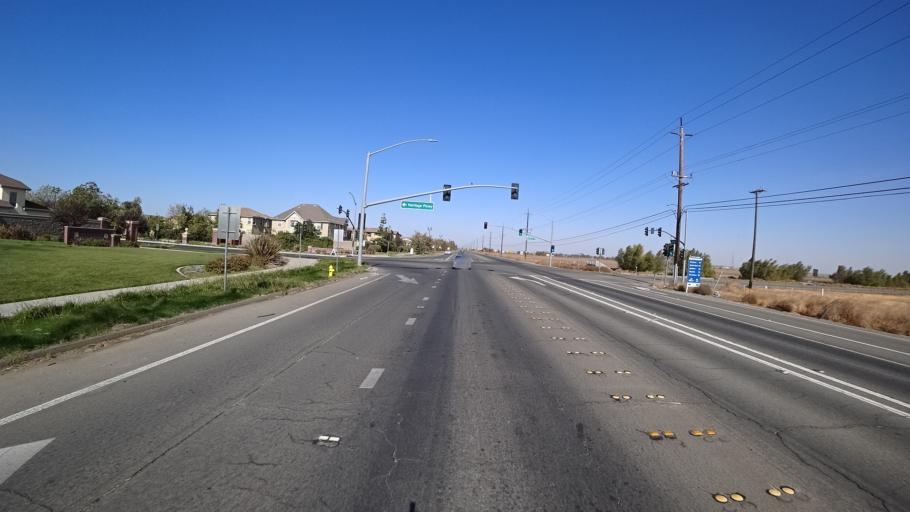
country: US
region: California
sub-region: Yolo County
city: Woodland
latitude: 38.6475
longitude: -121.7290
